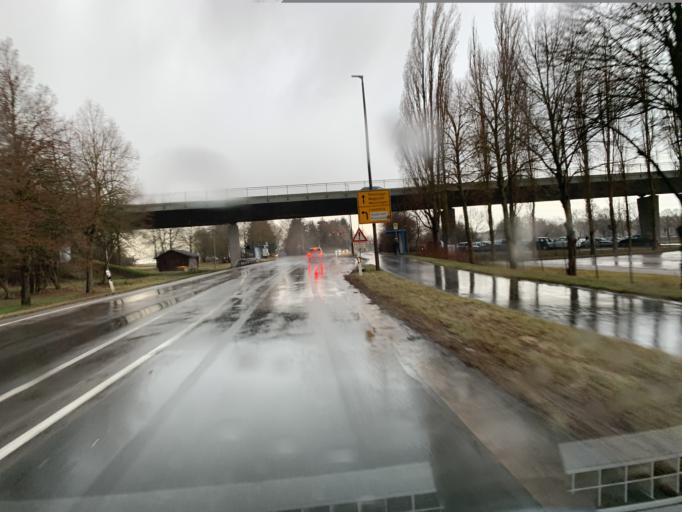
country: DE
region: Baden-Wuerttemberg
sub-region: Regierungsbezirk Stuttgart
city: Magstadt
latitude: 48.7103
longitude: 8.9815
